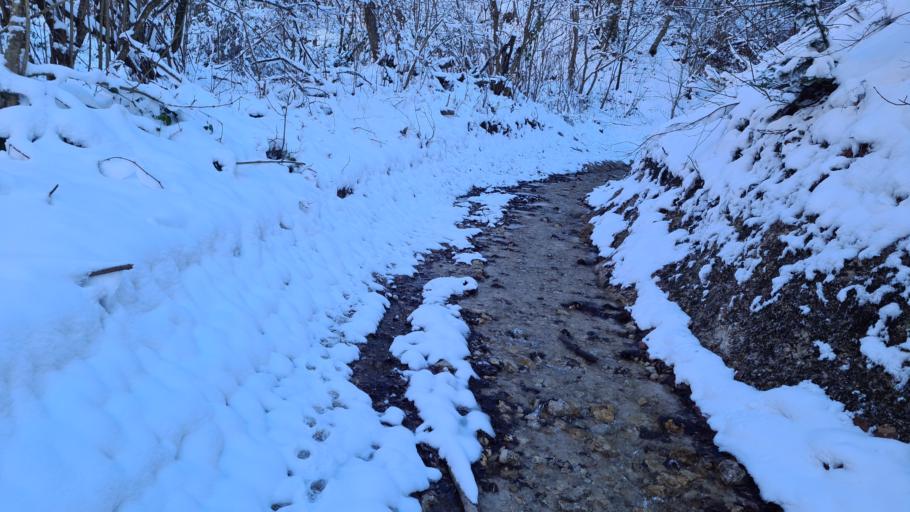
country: HR
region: Varazdinska
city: Lepoglava
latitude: 46.1825
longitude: 16.0730
